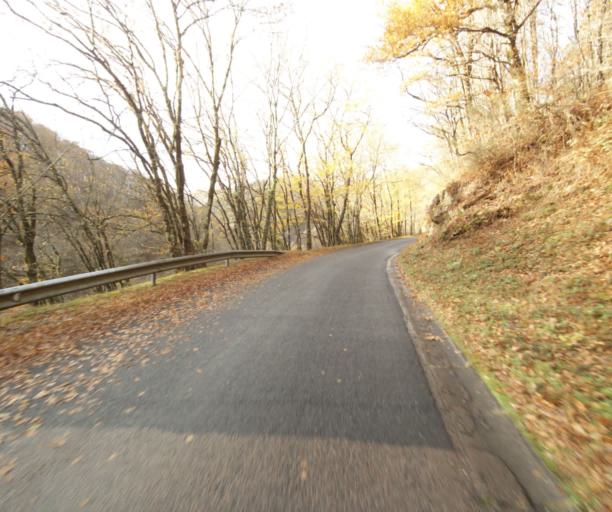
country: FR
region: Limousin
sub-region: Departement de la Correze
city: Cornil
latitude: 45.2166
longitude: 1.6940
